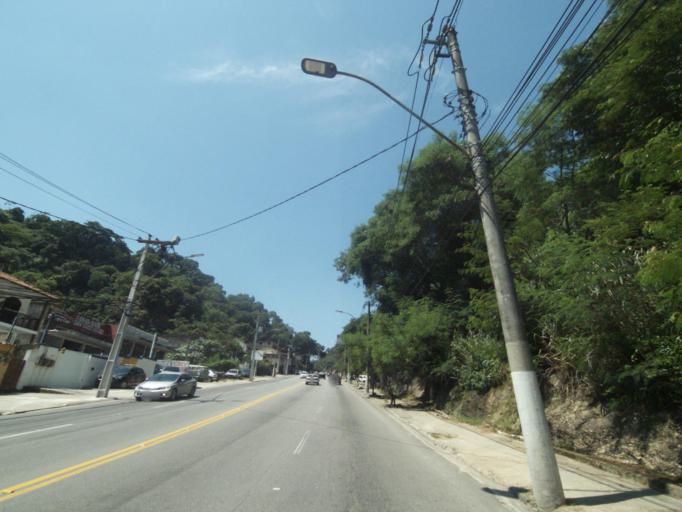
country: BR
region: Rio de Janeiro
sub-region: Niteroi
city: Niteroi
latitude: -22.9123
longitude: -43.0766
